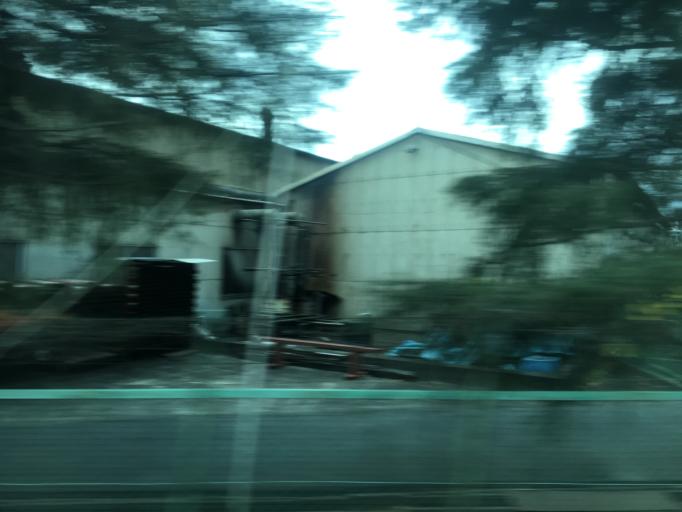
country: JP
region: Saitama
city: Okegawa
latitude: 36.0070
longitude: 139.5551
